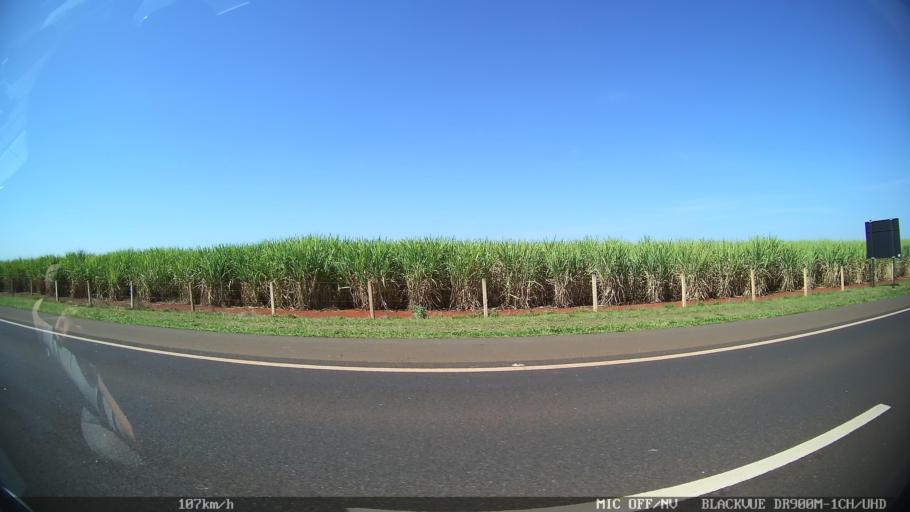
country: BR
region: Sao Paulo
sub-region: Batatais
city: Batatais
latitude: -20.7804
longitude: -47.5499
